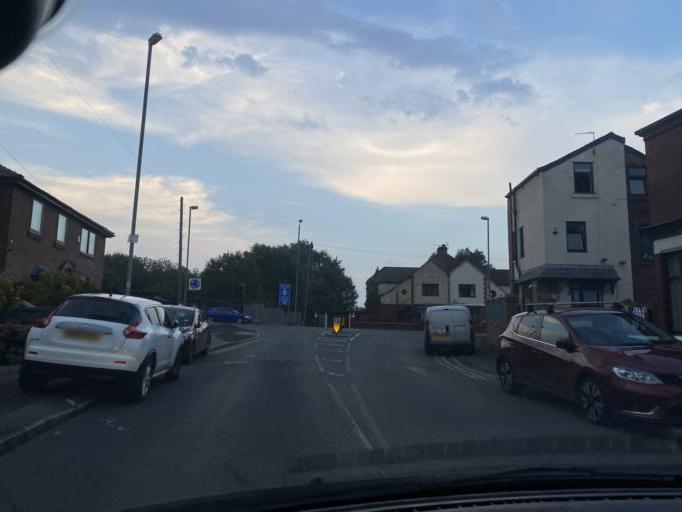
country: GB
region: England
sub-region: Borough of Tameside
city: Denton
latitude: 53.4684
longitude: -2.1205
